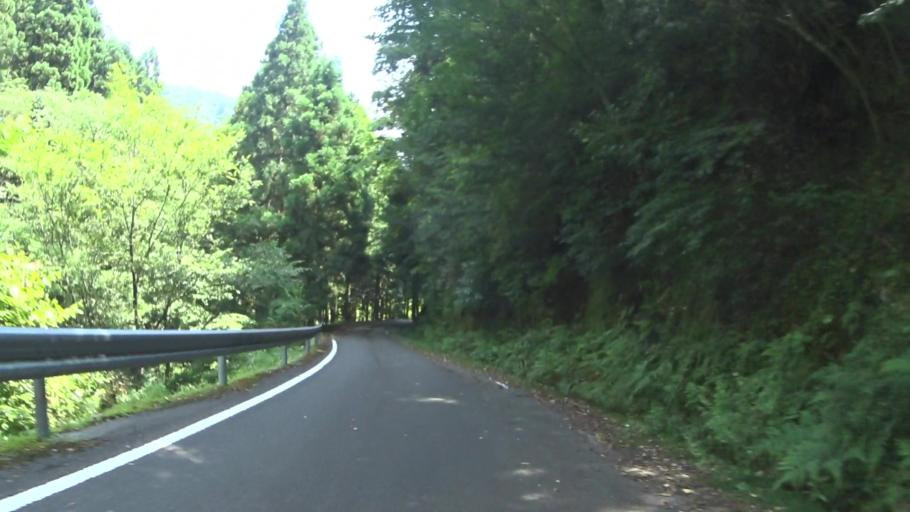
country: JP
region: Kyoto
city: Maizuru
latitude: 35.3501
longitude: 135.5200
